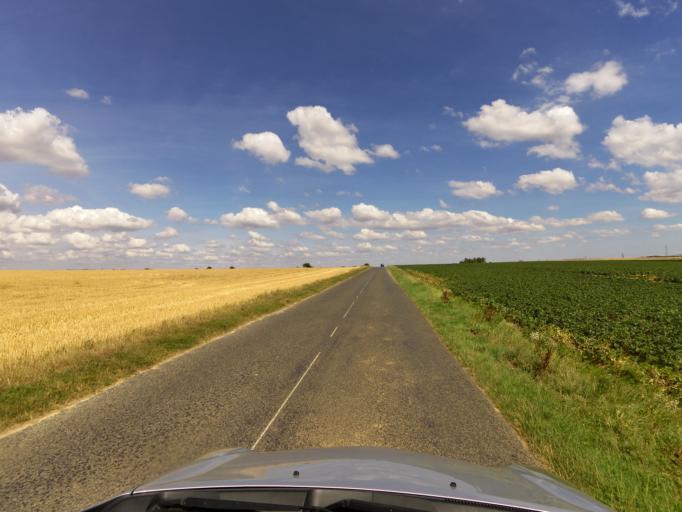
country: FR
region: Picardie
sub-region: Departement de l'Aisne
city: Courmelles
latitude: 49.3246
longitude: 3.2793
